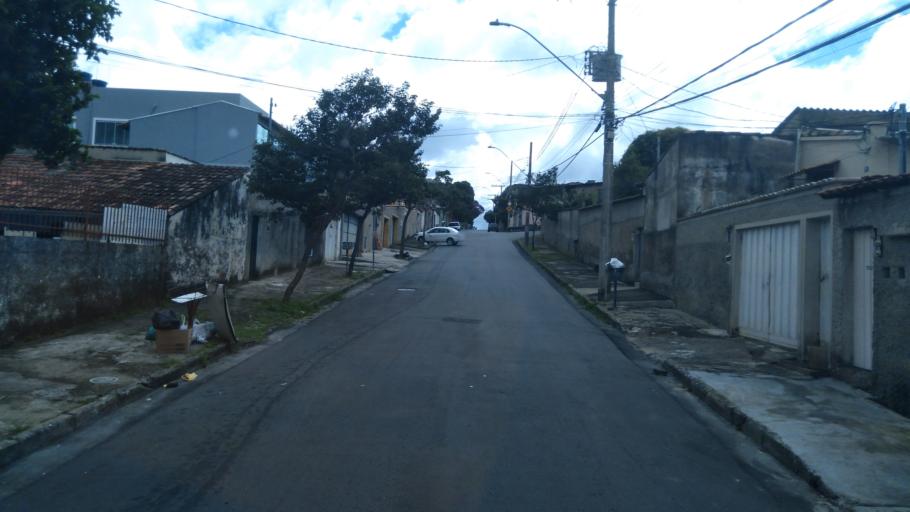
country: BR
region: Minas Gerais
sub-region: Belo Horizonte
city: Belo Horizonte
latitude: -19.8896
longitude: -43.8996
